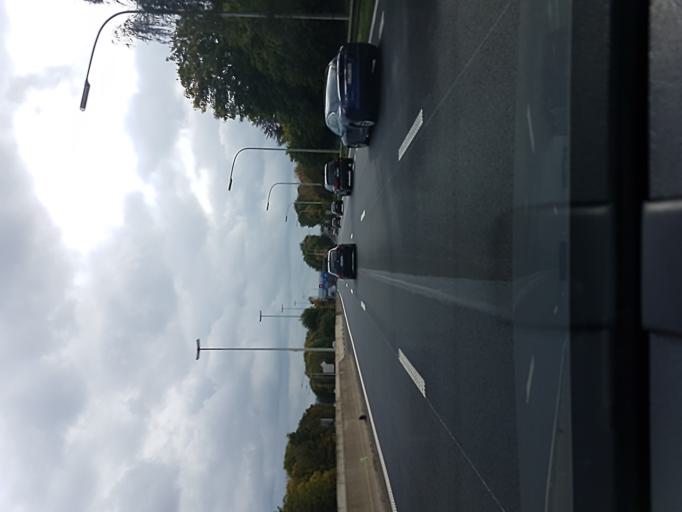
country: BE
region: Wallonia
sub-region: Province de Liege
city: Saint-Nicolas
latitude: 50.6437
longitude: 5.5449
